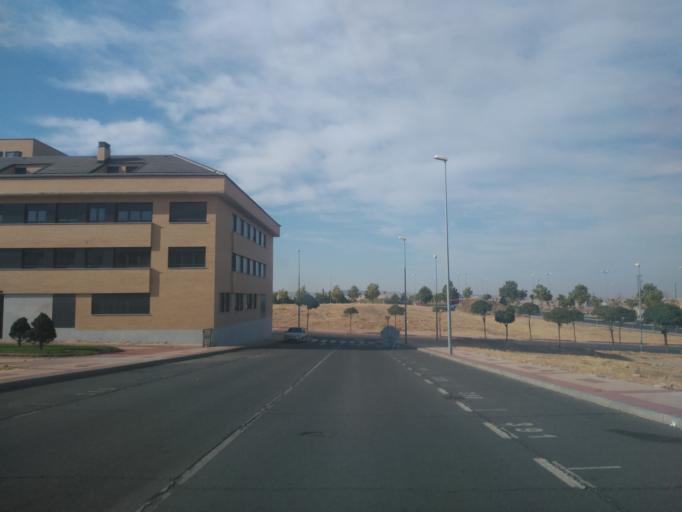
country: ES
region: Castille and Leon
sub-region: Provincia de Salamanca
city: Salamanca
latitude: 40.9773
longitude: -5.6826
